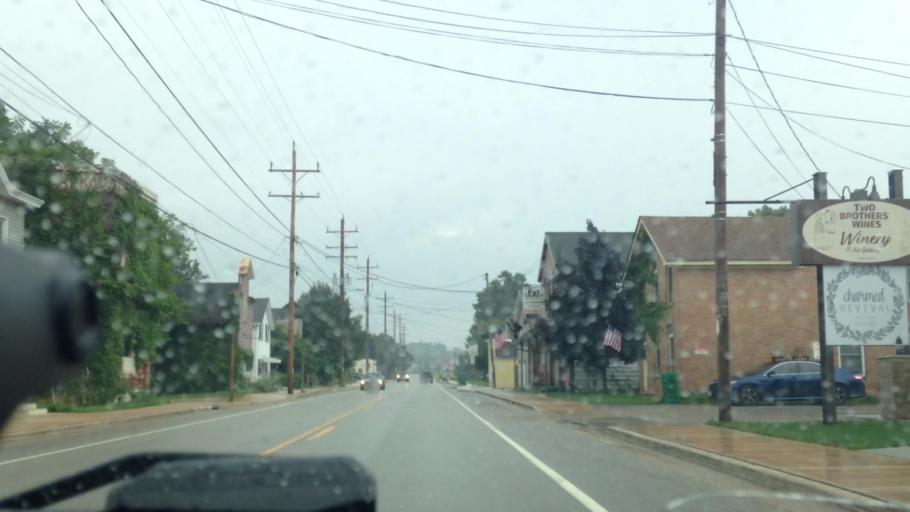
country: US
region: Wisconsin
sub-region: Washington County
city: Richfield
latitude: 43.2576
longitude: -88.1951
